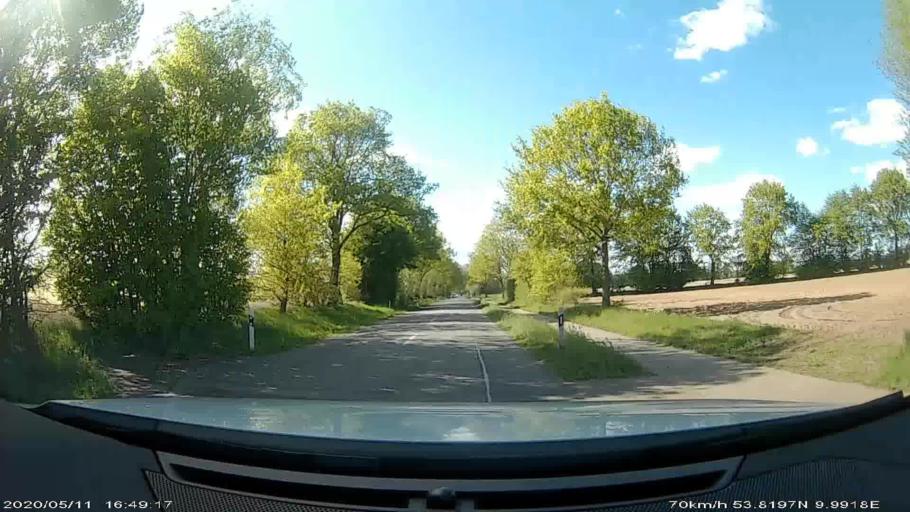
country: DE
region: Schleswig-Holstein
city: Oersdorf
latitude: 53.8272
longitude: 9.9821
